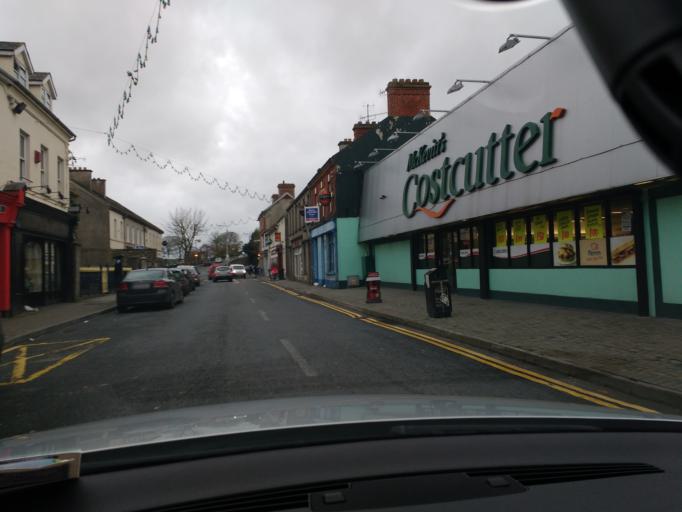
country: IE
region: Munster
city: Thurles
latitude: 52.6782
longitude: -7.8182
